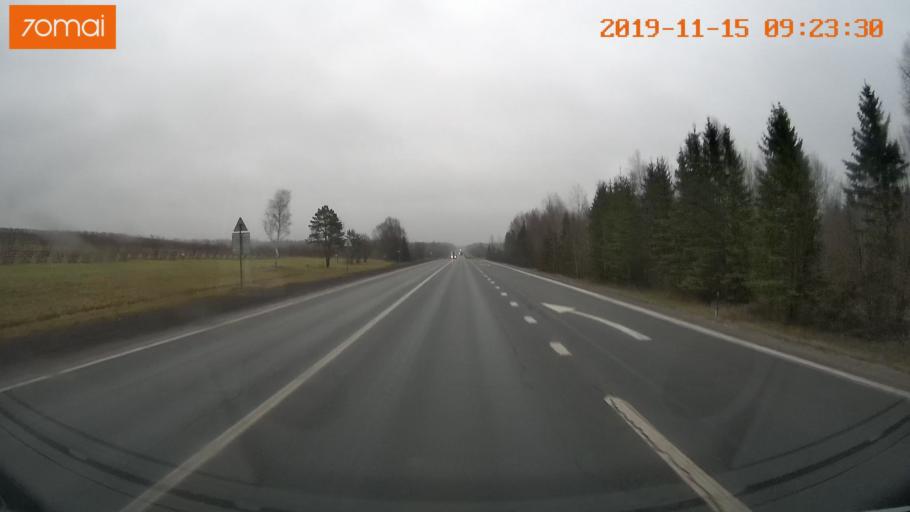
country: RU
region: Vologda
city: Tonshalovo
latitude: 59.3009
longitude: 38.1127
